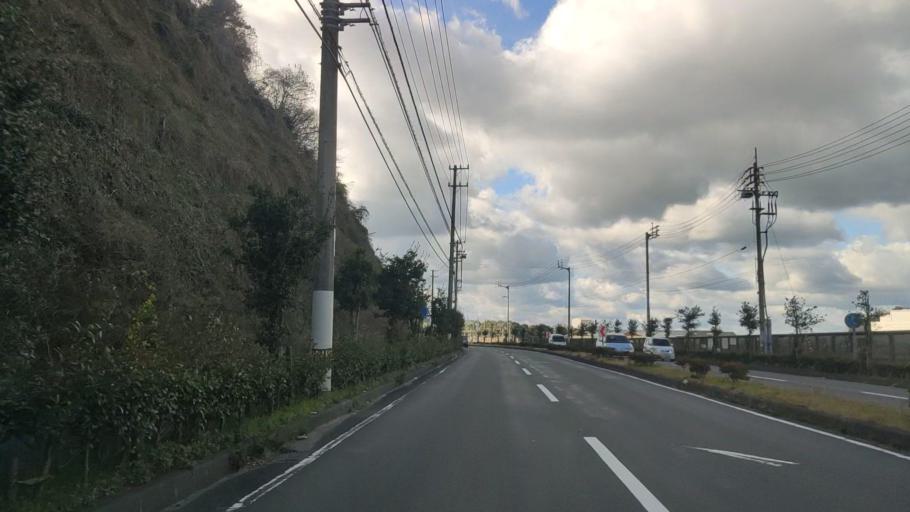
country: JP
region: Ehime
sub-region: Shikoku-chuo Shi
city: Matsuyama
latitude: 33.8456
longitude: 132.7099
